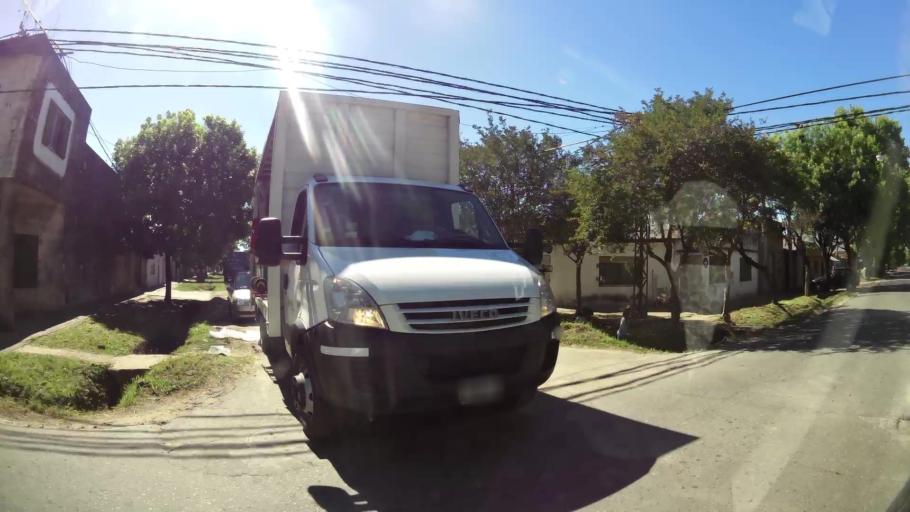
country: AR
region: Santa Fe
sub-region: Departamento de Rosario
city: Rosario
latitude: -32.9600
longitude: -60.6939
